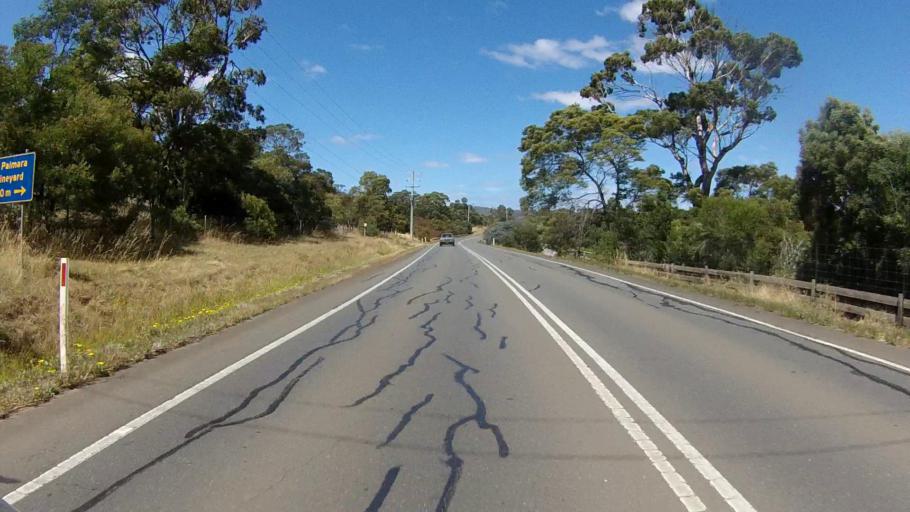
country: AU
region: Tasmania
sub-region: Clarence
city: Cambridge
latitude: -42.7445
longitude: 147.4192
